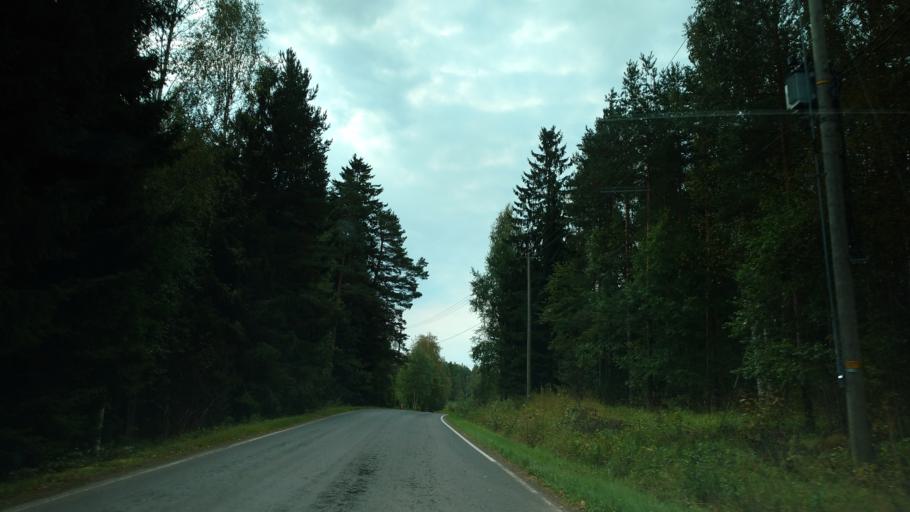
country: FI
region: Varsinais-Suomi
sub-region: Loimaa
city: Koski Tl
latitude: 60.7352
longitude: 23.1913
